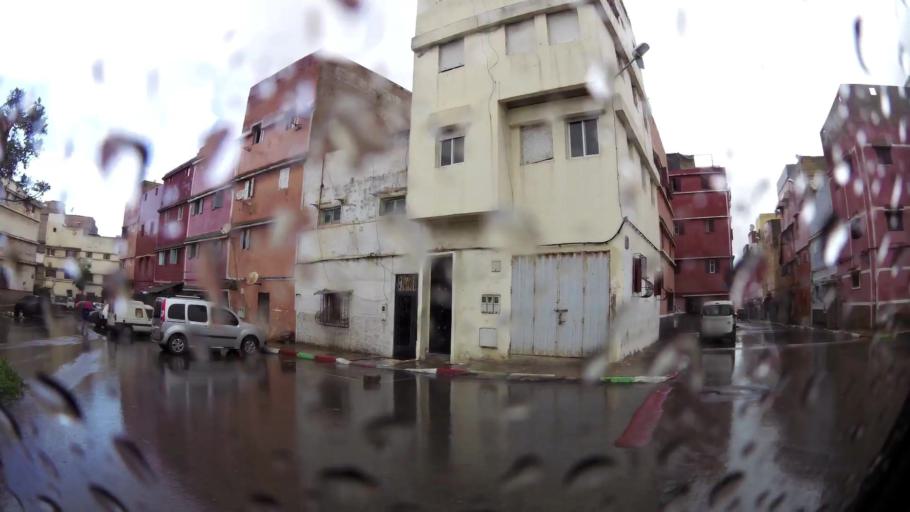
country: MA
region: Grand Casablanca
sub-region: Mediouna
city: Tit Mellil
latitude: 33.5541
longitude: -7.5496
